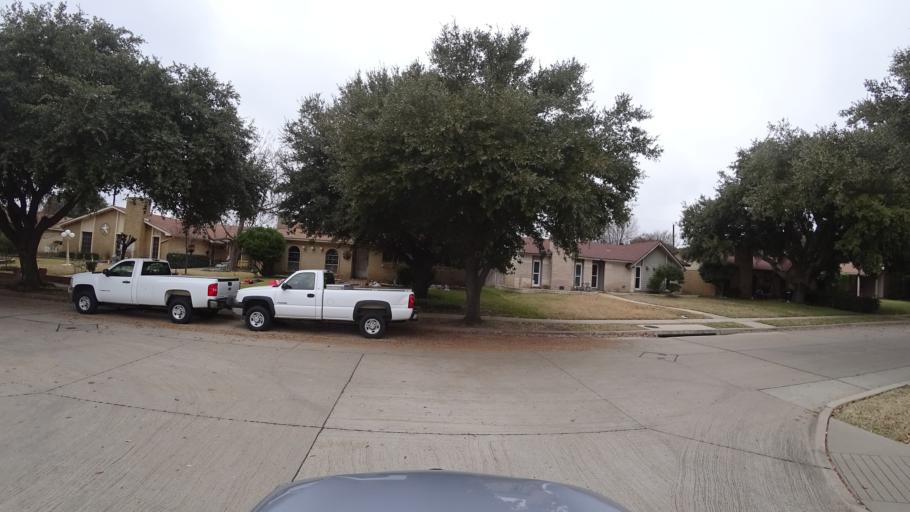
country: US
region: Texas
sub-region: Denton County
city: Lewisville
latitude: 33.0382
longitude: -97.0312
